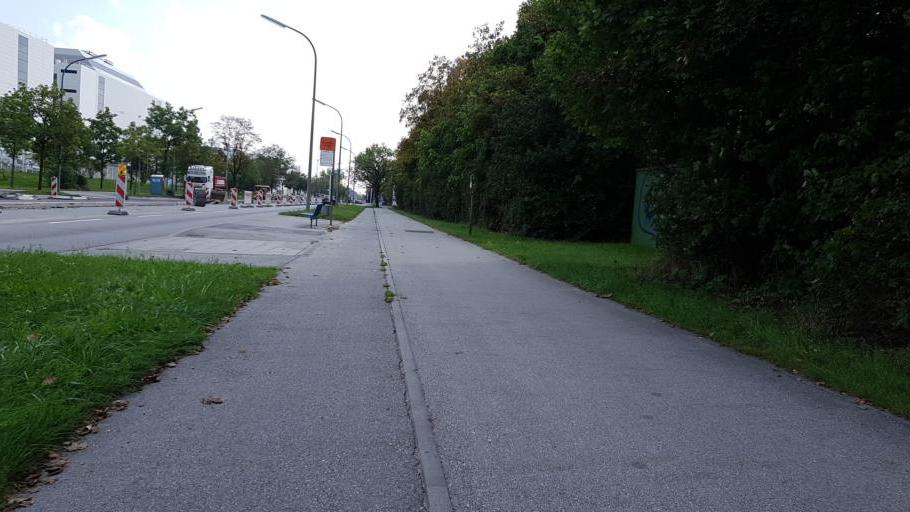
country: DE
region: Bavaria
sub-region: Upper Bavaria
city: Oberschleissheim
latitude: 48.1964
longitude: 11.5647
